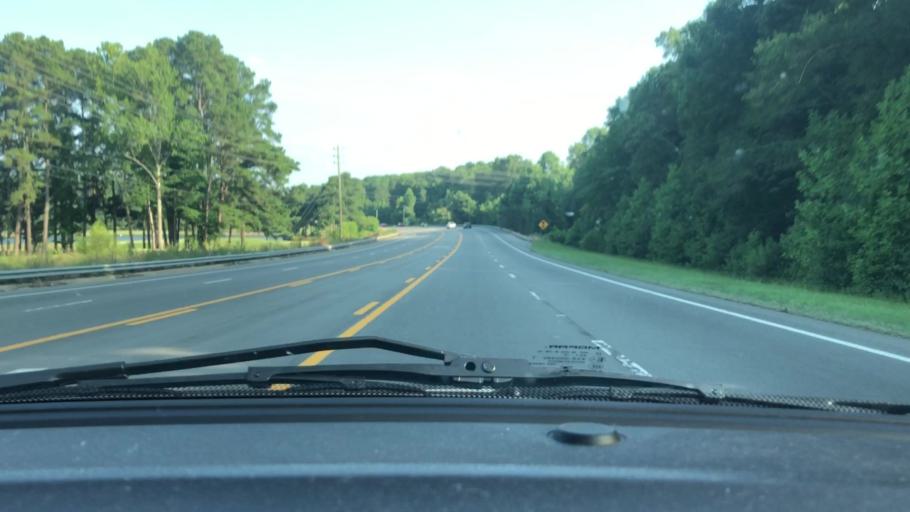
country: US
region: North Carolina
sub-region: Lee County
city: Broadway
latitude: 35.4033
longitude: -79.1143
